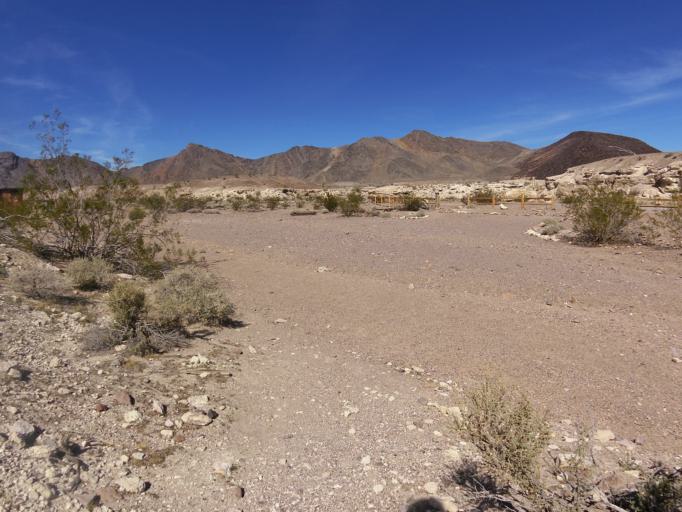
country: US
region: Nevada
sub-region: Nye County
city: Pahrump
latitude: 35.9730
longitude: -116.2741
